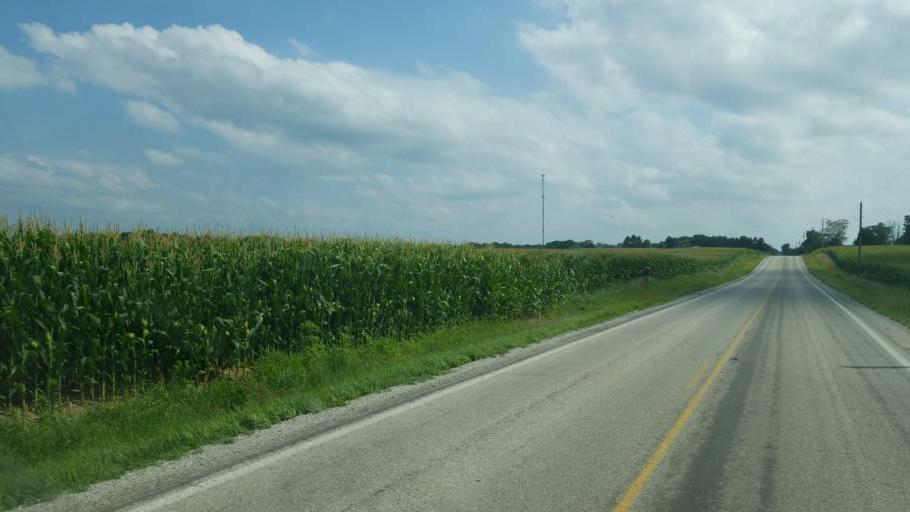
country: US
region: Ohio
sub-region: Crawford County
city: Crestline
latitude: 40.8436
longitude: -82.7837
